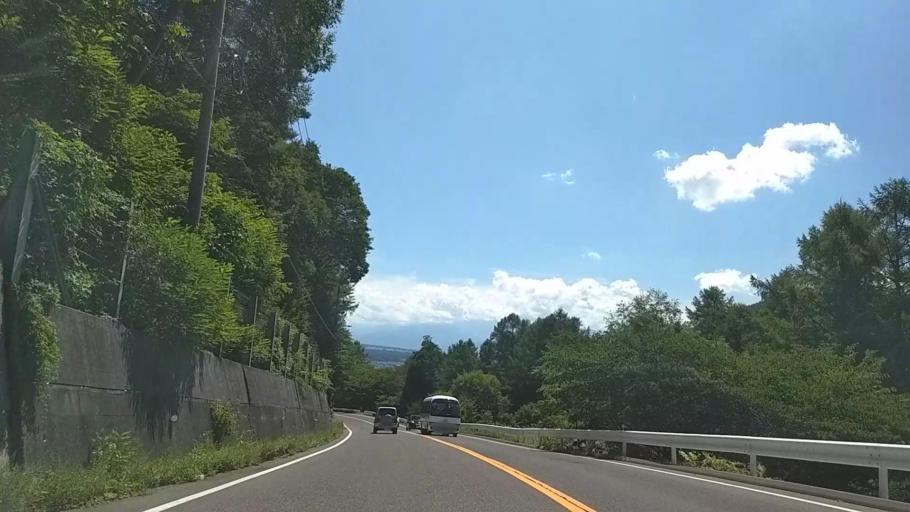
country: JP
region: Nagano
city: Chino
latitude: 36.0742
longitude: 138.2229
